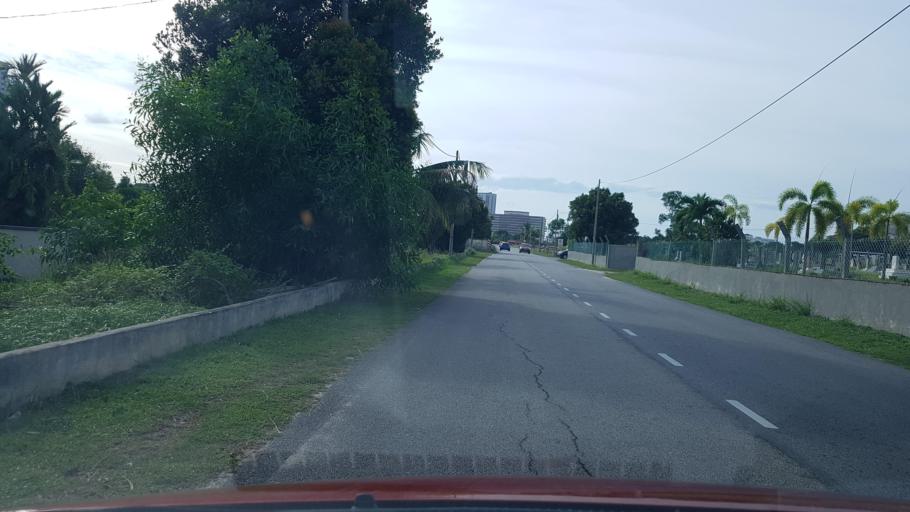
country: MY
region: Terengganu
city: Kuala Terengganu
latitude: 5.3201
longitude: 103.1469
